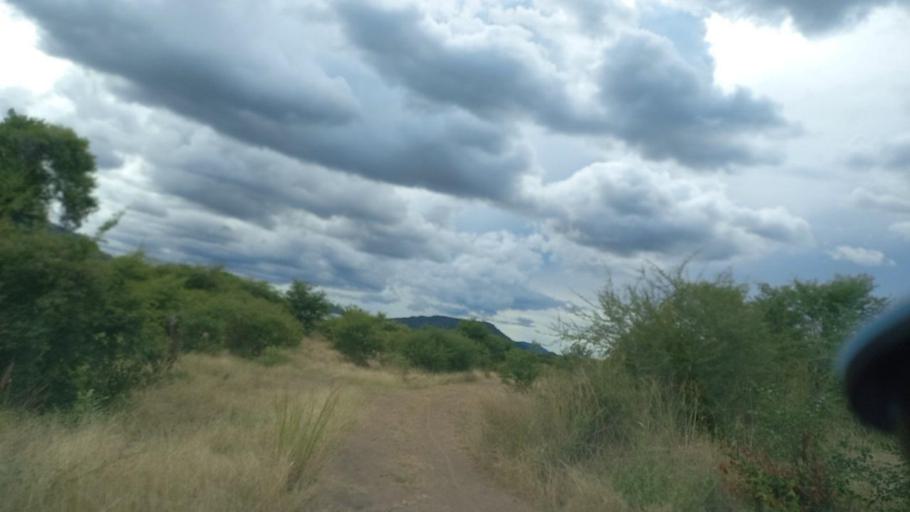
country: ZM
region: Lusaka
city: Luangwa
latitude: -15.6472
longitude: 30.3352
